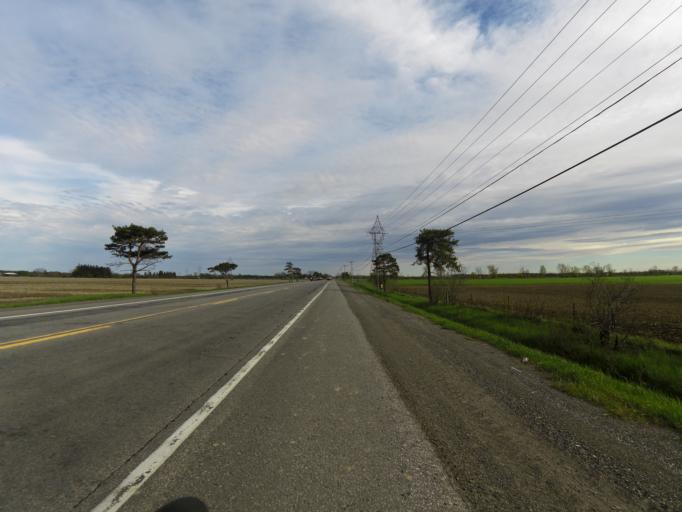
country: CA
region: Ontario
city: Ottawa
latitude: 45.3147
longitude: -75.7127
